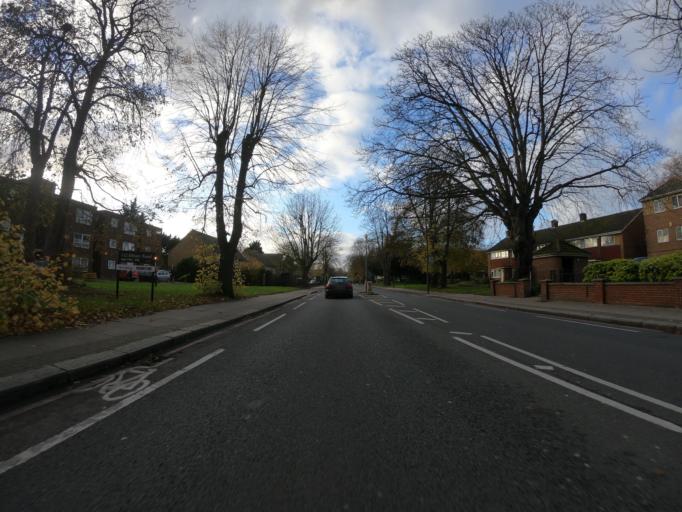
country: GB
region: England
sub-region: Greater London
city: Blackheath
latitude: 51.4537
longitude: 0.0248
